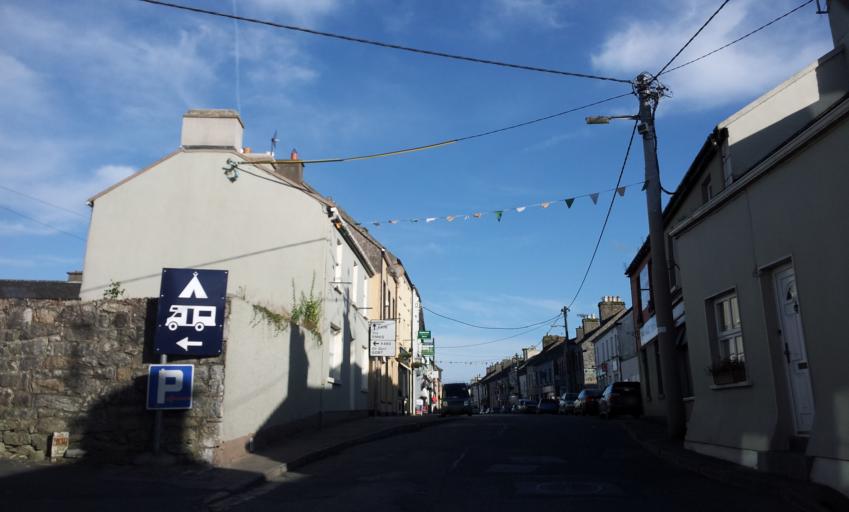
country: IE
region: Munster
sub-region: An Clar
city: Ennis
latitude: 52.9455
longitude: -9.0654
